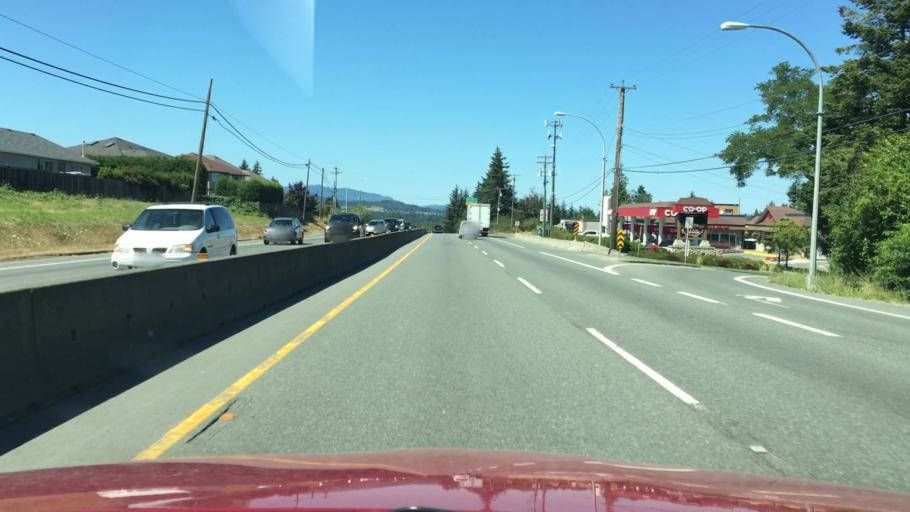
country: CA
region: British Columbia
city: North Saanich
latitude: 48.5562
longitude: -123.3934
